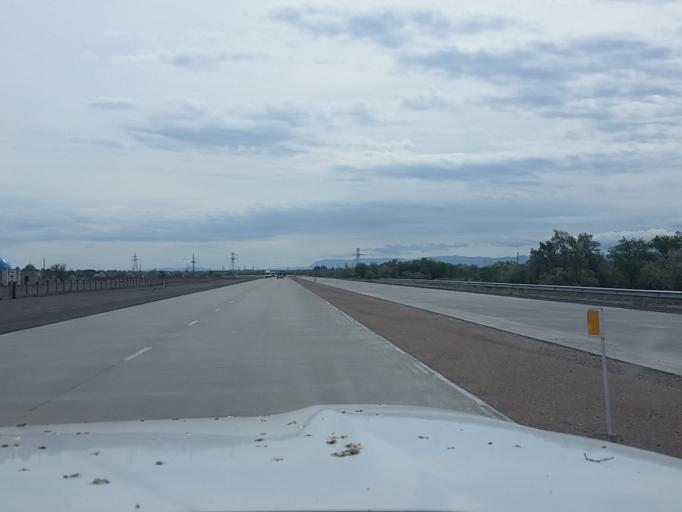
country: KZ
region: Almaty Oblysy
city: Turgen'
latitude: 43.5784
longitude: 78.1958
